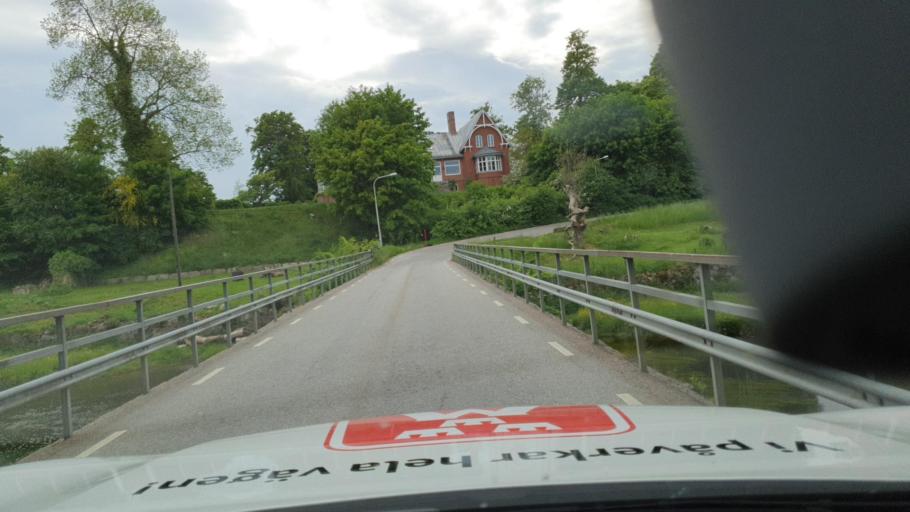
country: SE
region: Skane
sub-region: Ystads Kommun
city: Kopingebro
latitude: 55.4806
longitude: 13.9409
